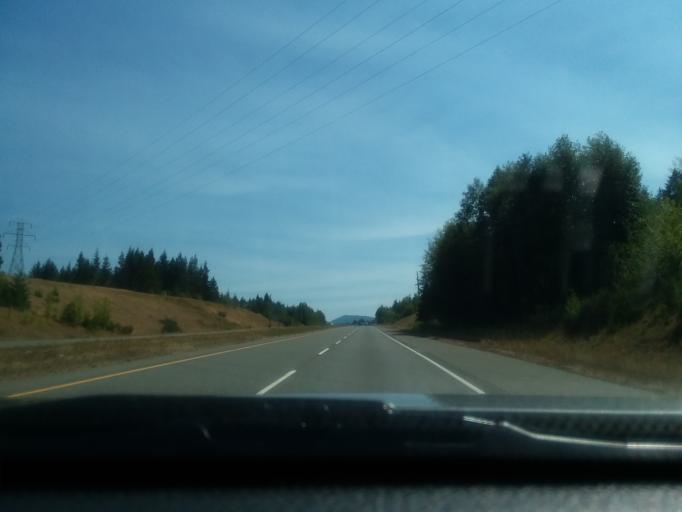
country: CA
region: British Columbia
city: Port Alberni
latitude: 49.3808
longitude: -124.6264
